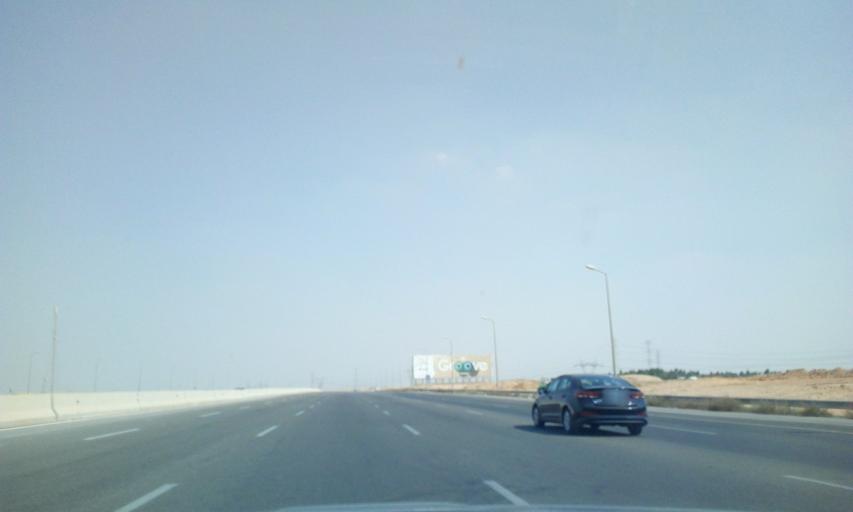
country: EG
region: Muhafazat al Qahirah
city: Halwan
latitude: 29.9096
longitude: 31.6447
